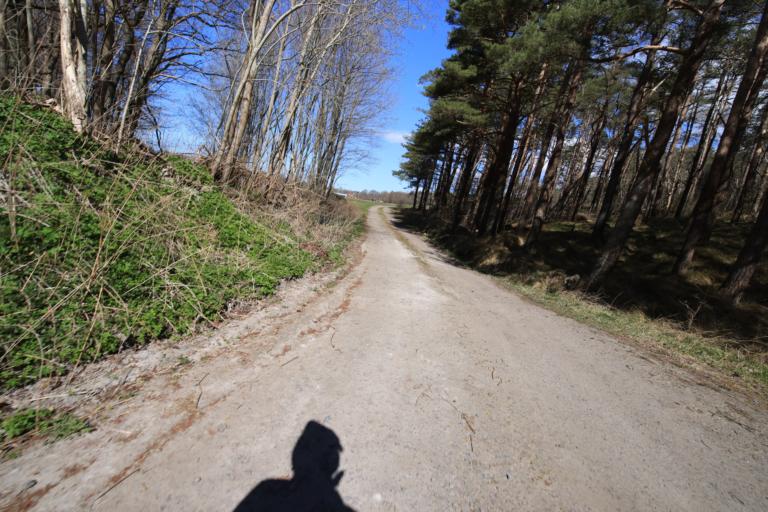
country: SE
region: Halland
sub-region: Varbergs Kommun
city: Varberg
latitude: 57.1837
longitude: 12.2302
